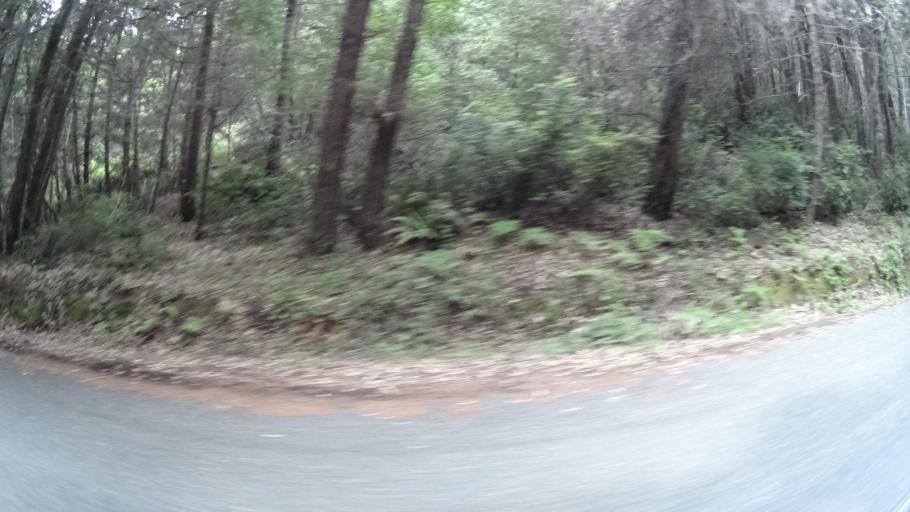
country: US
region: California
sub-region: Humboldt County
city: Willow Creek
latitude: 41.1977
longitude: -123.7590
